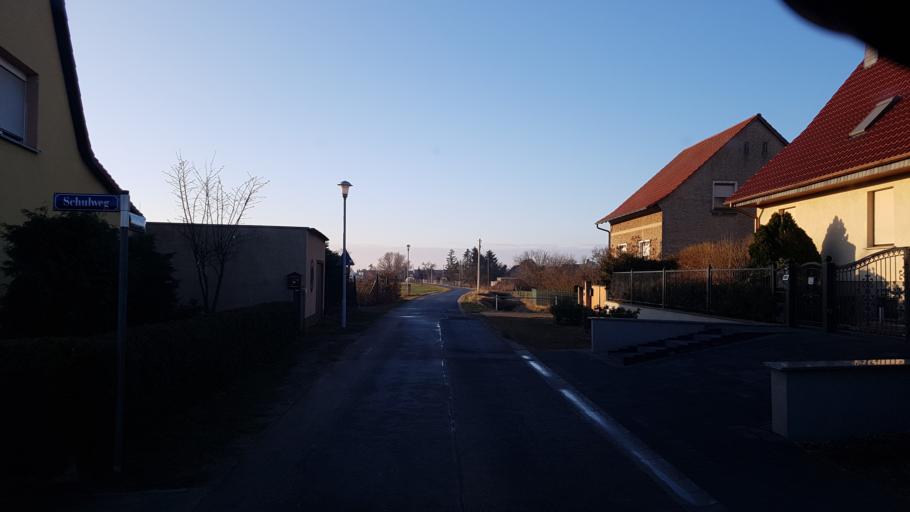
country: DE
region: Brandenburg
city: Falkenberg
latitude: 51.5829
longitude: 13.2115
